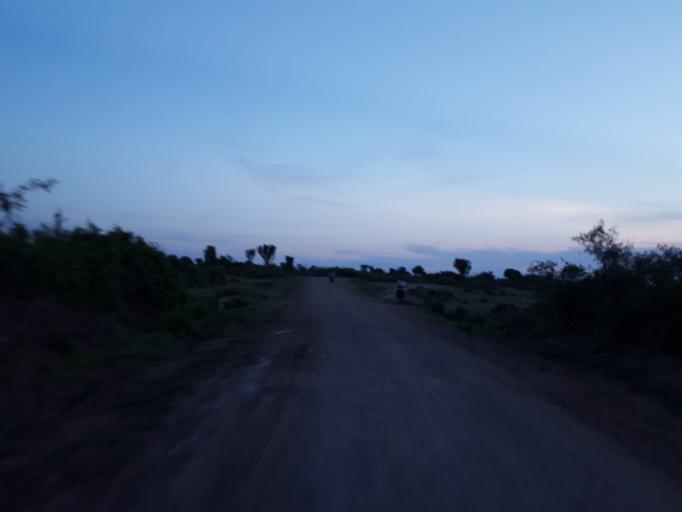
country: UG
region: Western Region
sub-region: Kibale District
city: Kagadi
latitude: 1.2384
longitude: 30.7445
